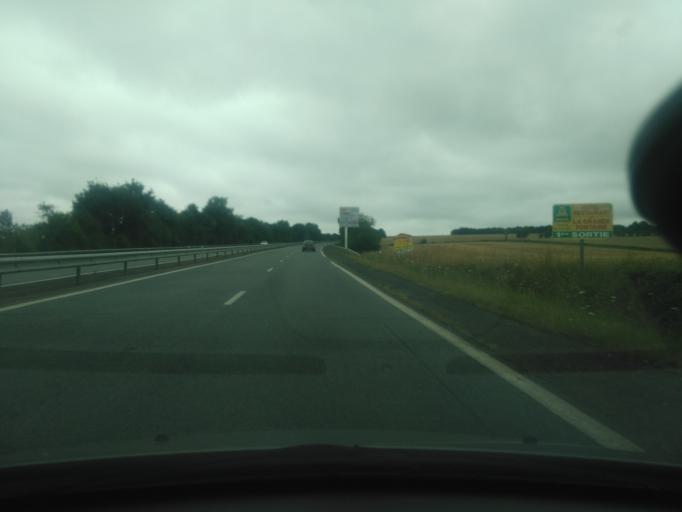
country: FR
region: Brittany
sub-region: Departement des Cotes-d'Armor
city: Jugon-les-Lacs
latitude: 48.4126
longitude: -2.3264
